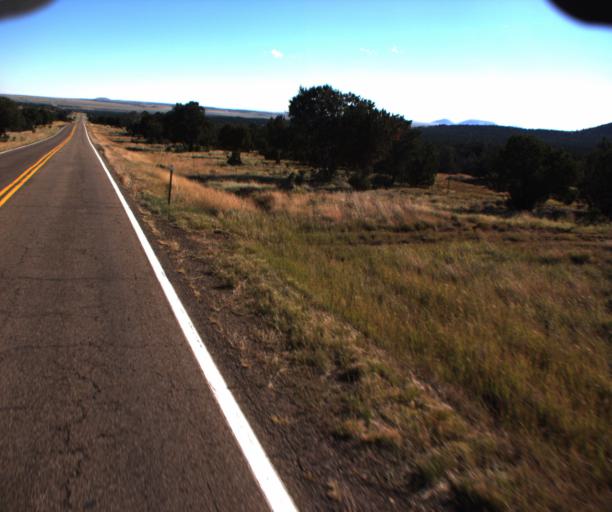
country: US
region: Arizona
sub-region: Navajo County
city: White Mountain Lake
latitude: 34.3189
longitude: -109.7631
